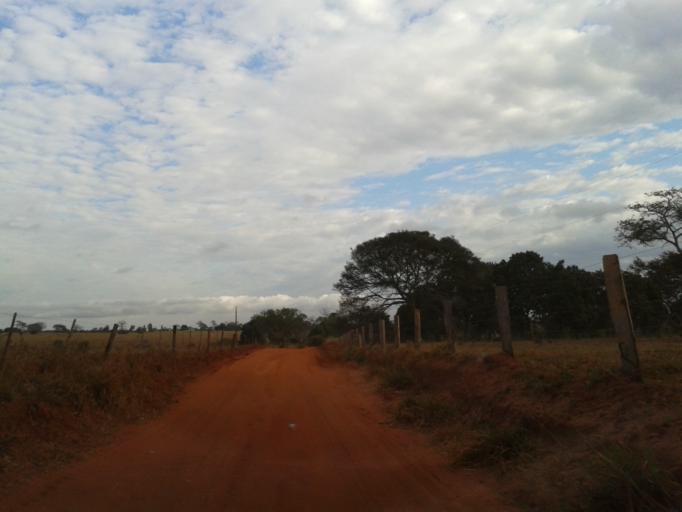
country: BR
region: Minas Gerais
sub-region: Santa Vitoria
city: Santa Vitoria
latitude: -18.7644
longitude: -50.1889
